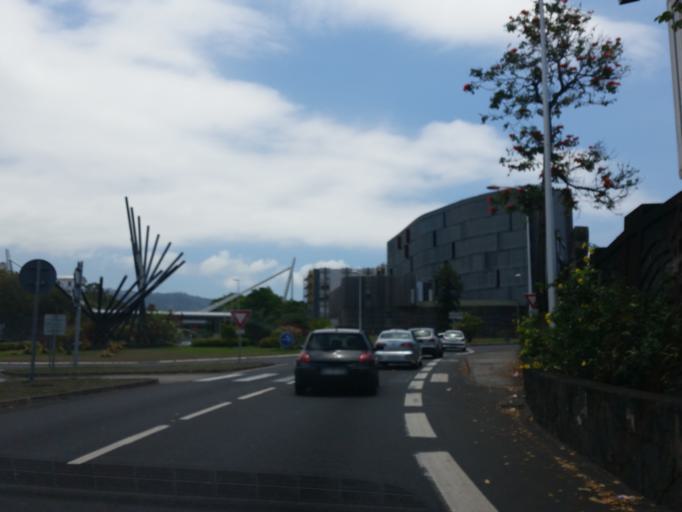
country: RE
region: Reunion
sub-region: Reunion
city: Saint-Denis
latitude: -20.9008
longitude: 55.4880
